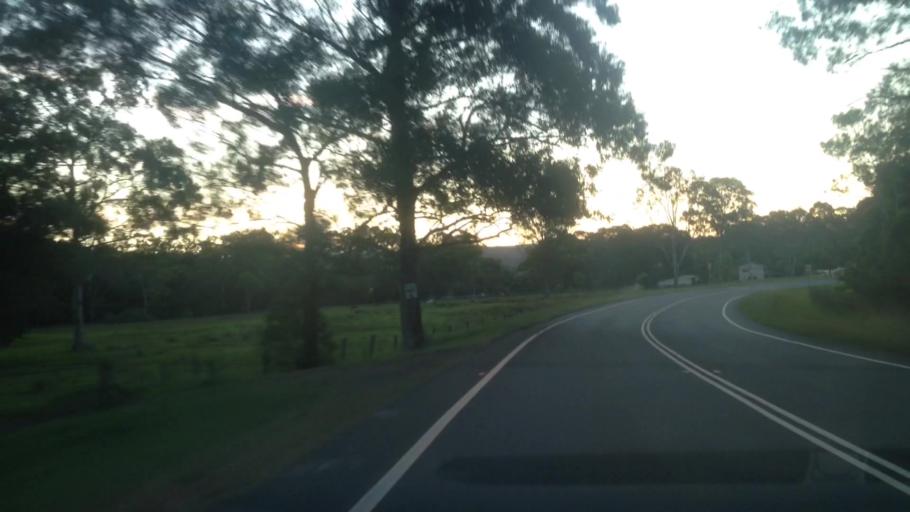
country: AU
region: New South Wales
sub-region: Lake Macquarie Shire
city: Cooranbong
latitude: -33.0717
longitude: 151.4692
